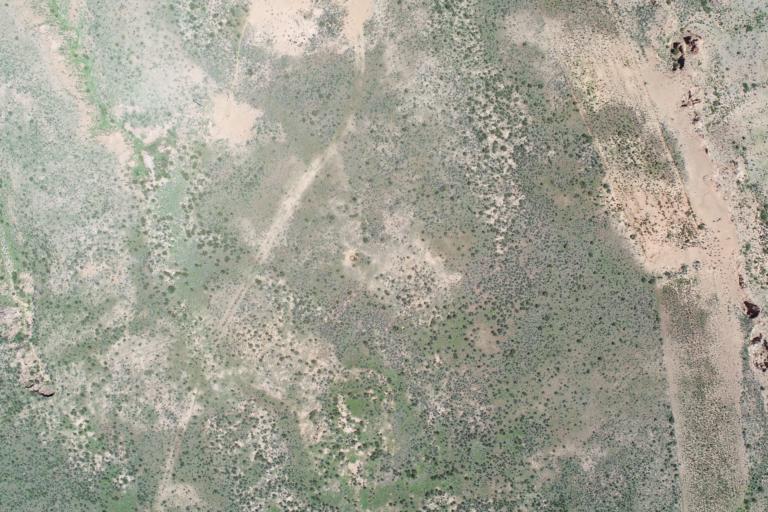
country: BO
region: La Paz
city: Curahuara de Carangas
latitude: -17.3241
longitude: -68.5078
